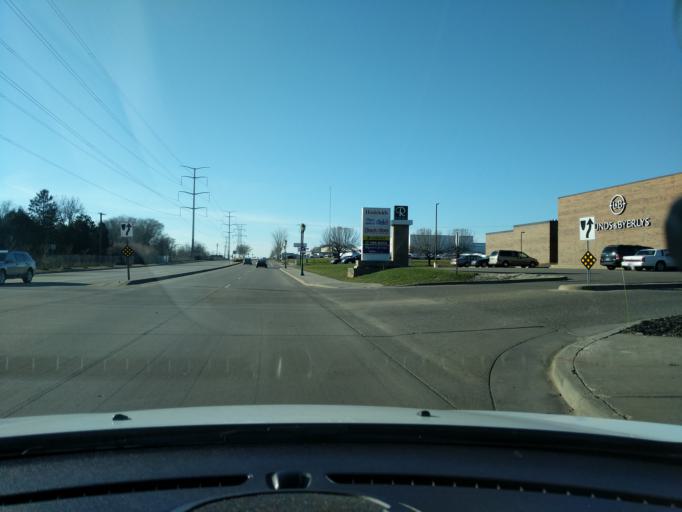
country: US
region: Minnesota
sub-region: Ramsey County
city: Roseville
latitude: 45.0212
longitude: -93.1698
